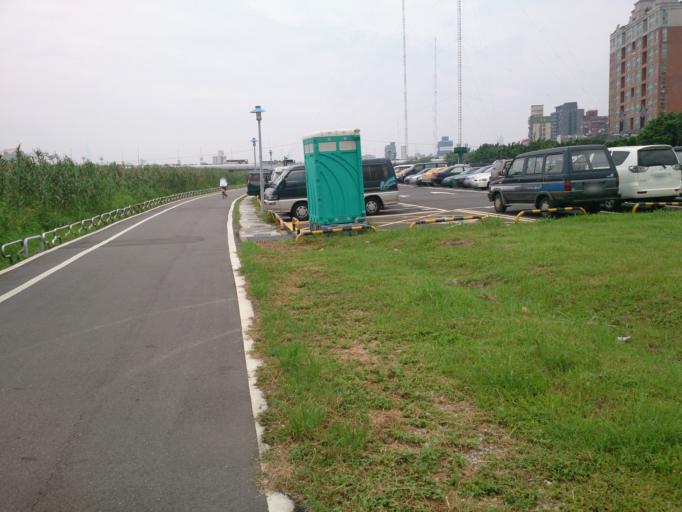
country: TW
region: Taipei
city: Taipei
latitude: 25.0916
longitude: 121.5118
